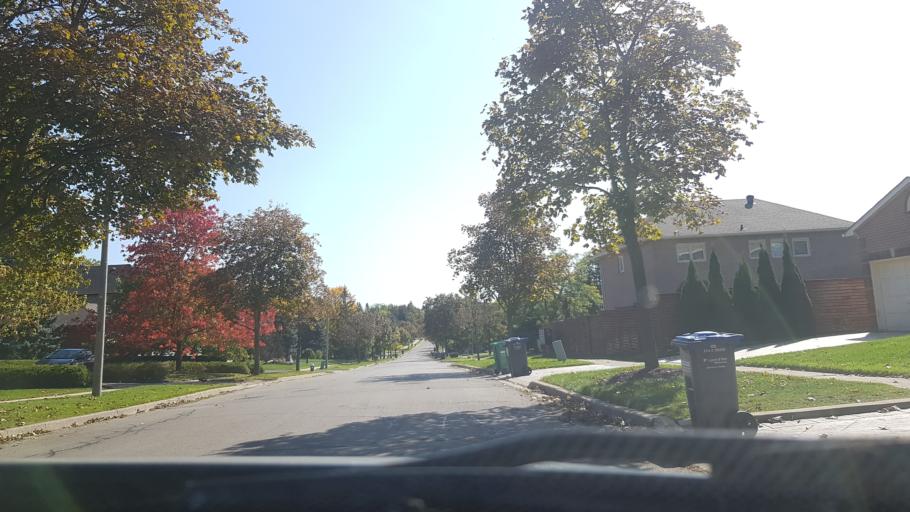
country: CA
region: Ontario
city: Brampton
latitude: 43.7425
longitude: -79.8046
